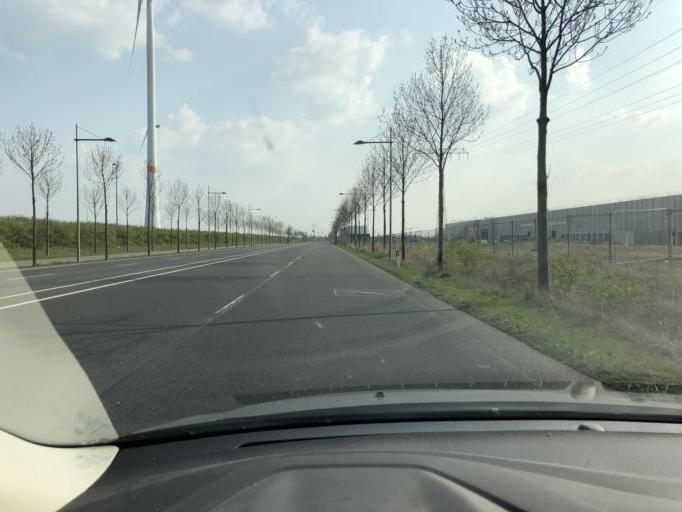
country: DE
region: Saxony
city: Rackwitz
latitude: 51.4064
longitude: 12.4322
